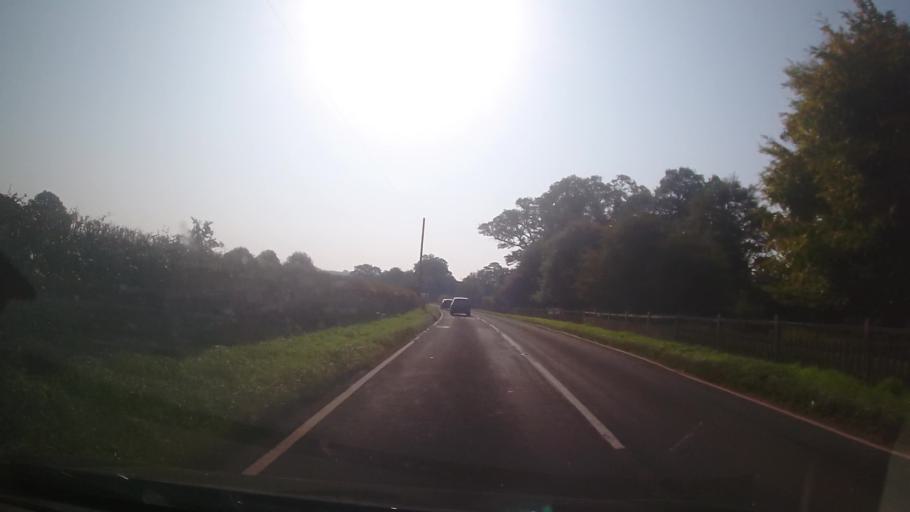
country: GB
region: England
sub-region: Shropshire
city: Alveley
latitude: 52.4971
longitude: -2.3690
